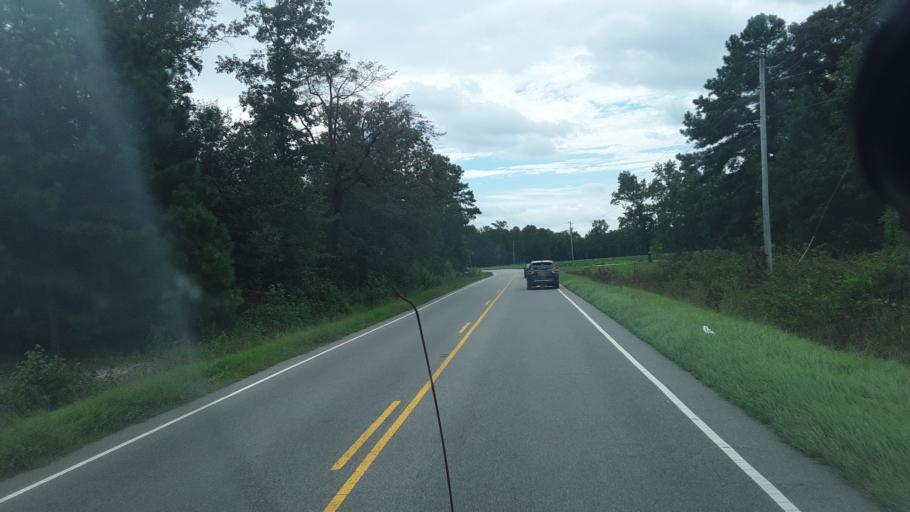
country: US
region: North Carolina
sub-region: Robeson County
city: Rowland
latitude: 34.6078
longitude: -79.3320
